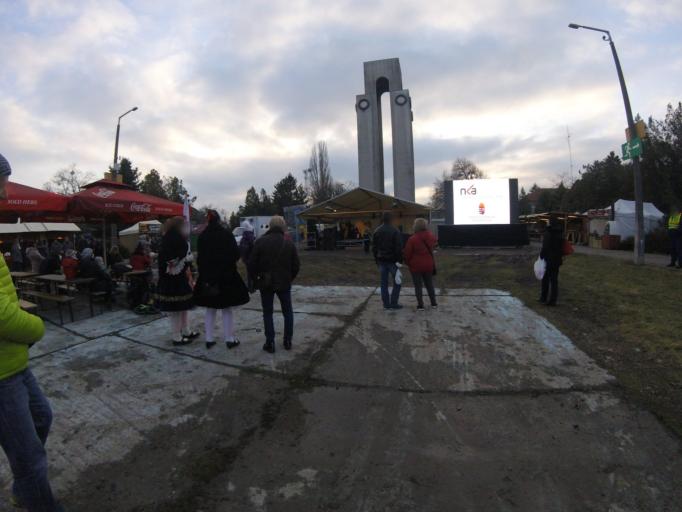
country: HU
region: Baranya
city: Mohacs
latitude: 45.9899
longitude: 18.6849
